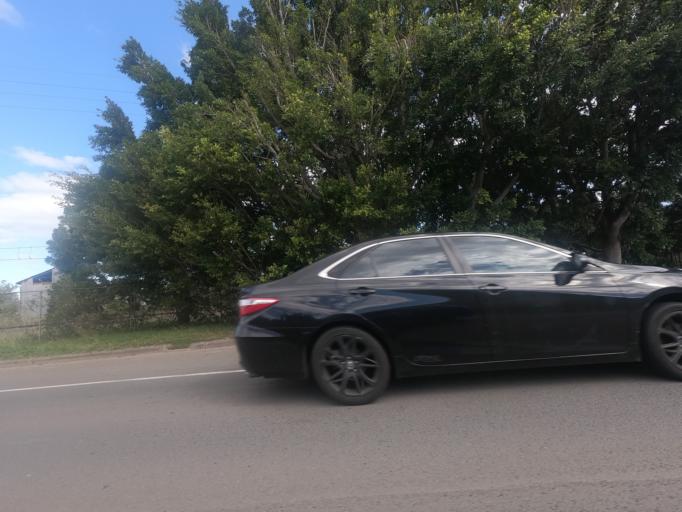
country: AU
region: New South Wales
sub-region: Wollongong
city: Koonawarra
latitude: -34.4707
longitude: 150.8151
